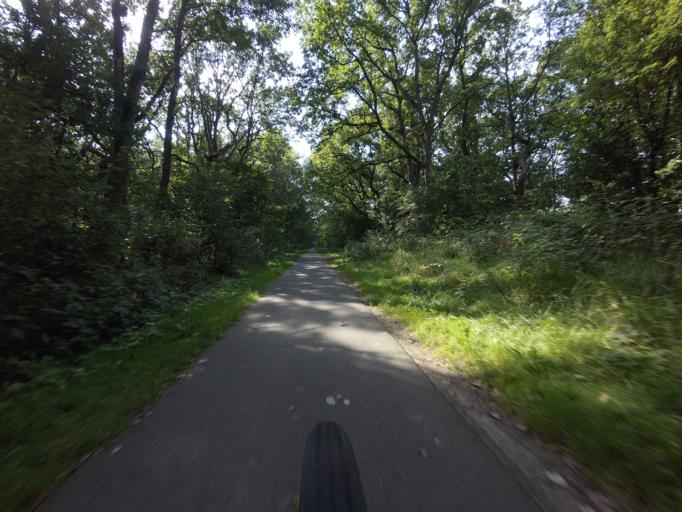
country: DK
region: Central Jutland
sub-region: Viborg Kommune
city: Viborg
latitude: 56.4071
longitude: 9.3588
